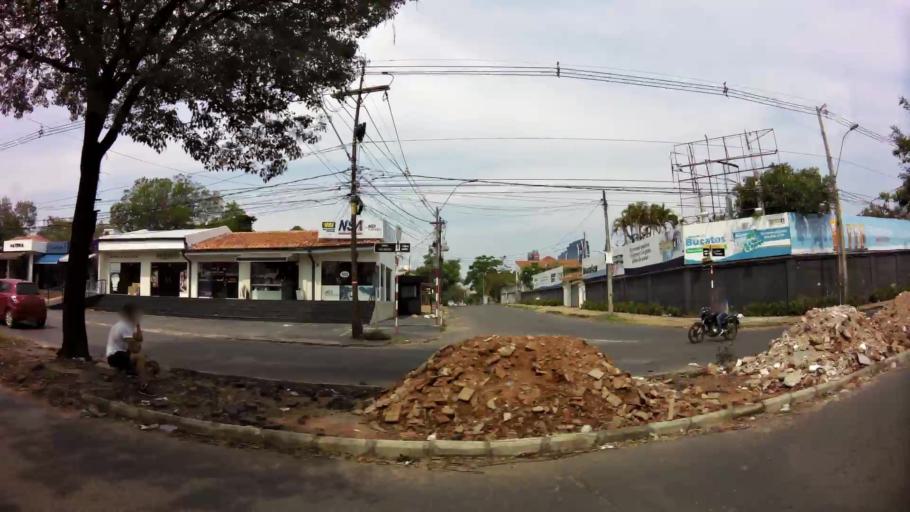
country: PY
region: Asuncion
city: Asuncion
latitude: -25.2810
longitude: -57.5710
